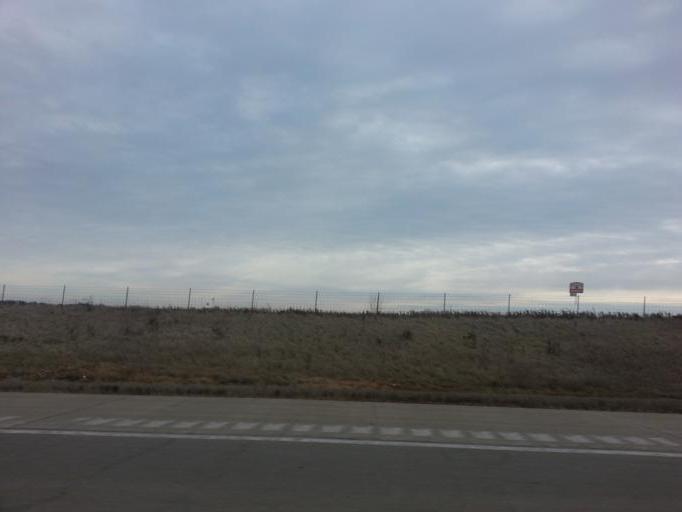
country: US
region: Illinois
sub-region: Woodford County
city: El Paso
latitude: 40.7939
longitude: -89.0352
